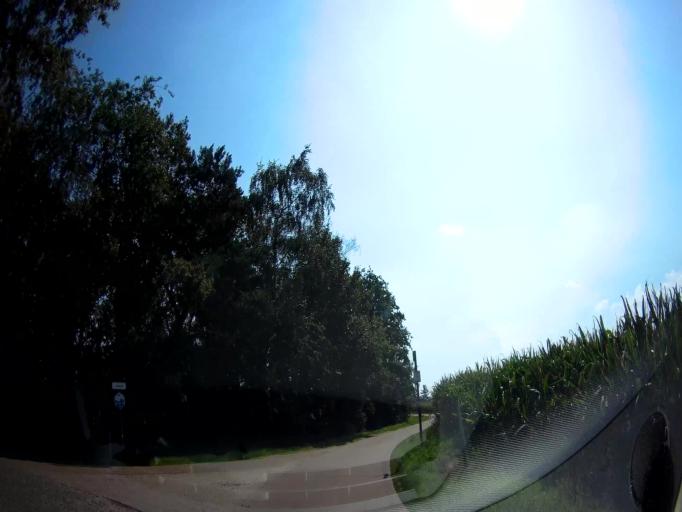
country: BE
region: Flanders
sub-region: Provincie Antwerpen
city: Retie
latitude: 51.2726
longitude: 5.0264
